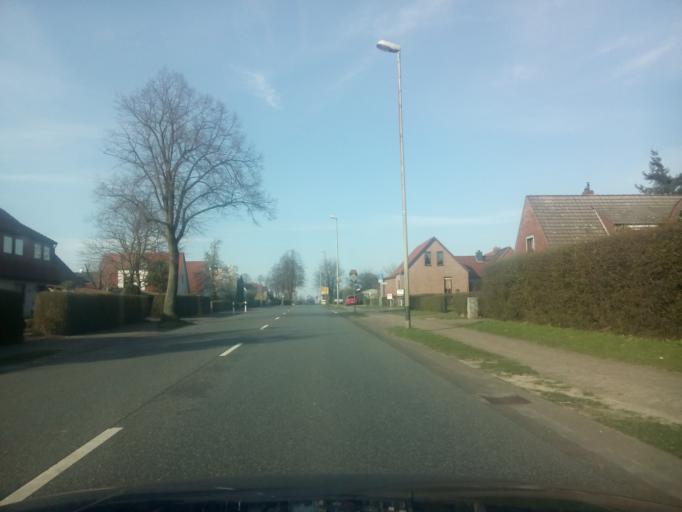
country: DE
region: Lower Saxony
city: Ritterhude
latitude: 53.1919
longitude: 8.7496
